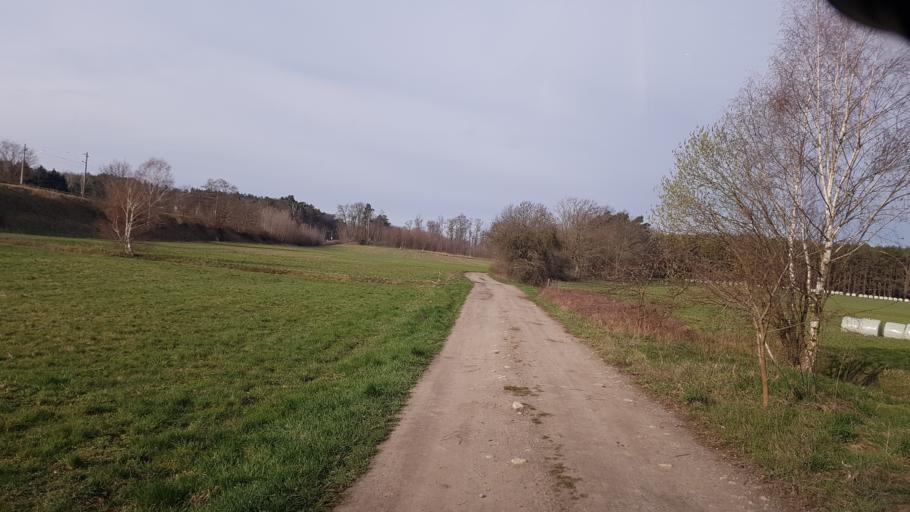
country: DE
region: Brandenburg
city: Bronkow
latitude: 51.6994
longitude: 13.8724
